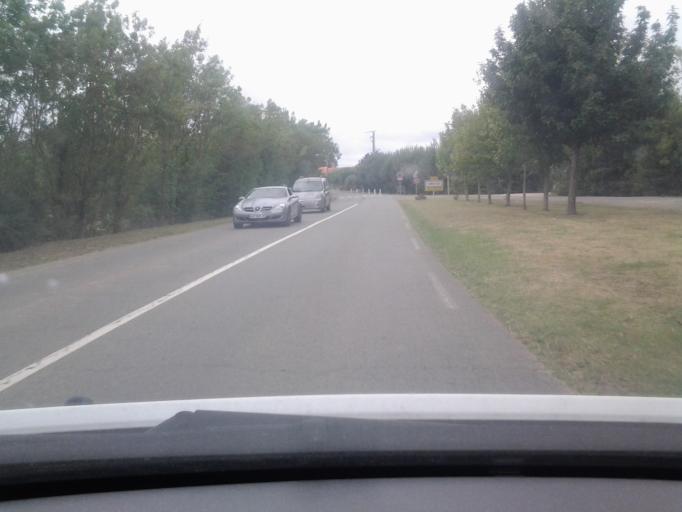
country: FR
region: Pays de la Loire
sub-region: Departement de la Vendee
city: Angles
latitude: 46.3932
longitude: -1.4048
